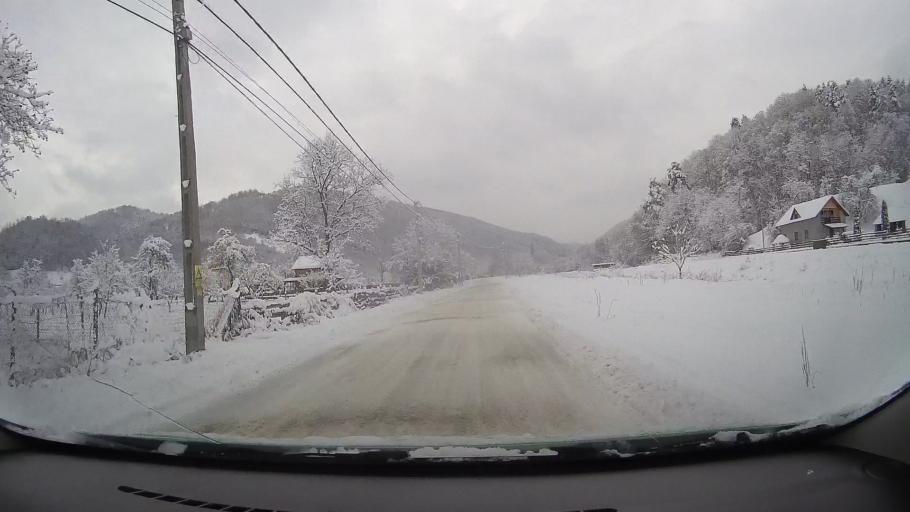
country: RO
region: Alba
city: Pianu de Sus
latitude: 45.8880
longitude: 23.4878
